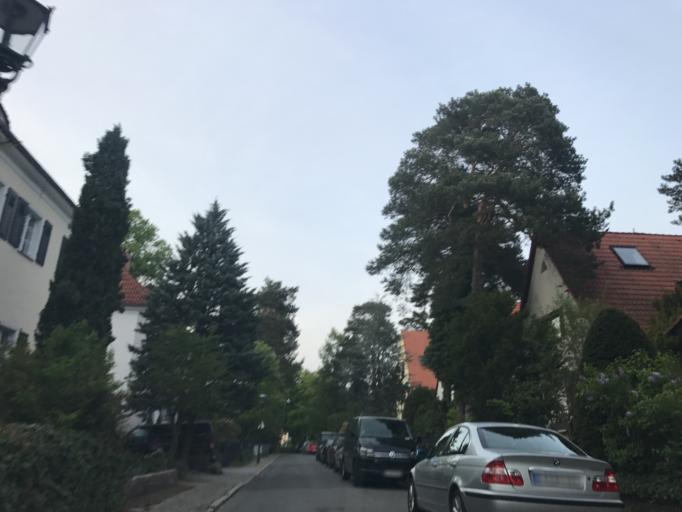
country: DE
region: Berlin
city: Grunewald
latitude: 52.5022
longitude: 13.2603
